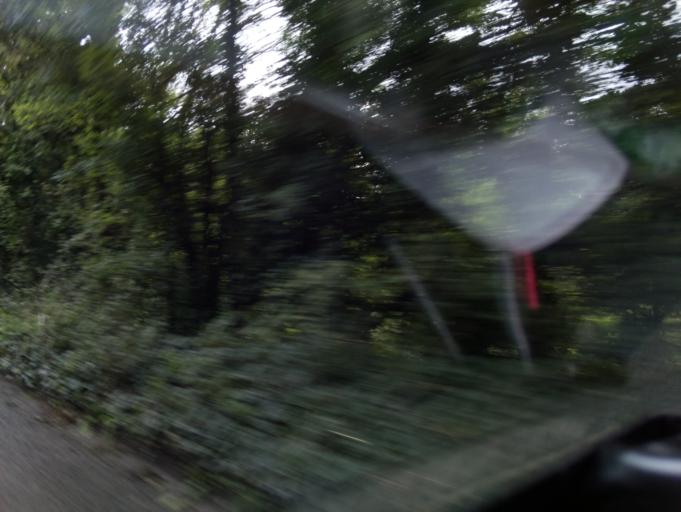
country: GB
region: England
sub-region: Devon
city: Modbury
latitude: 50.3467
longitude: -3.8888
